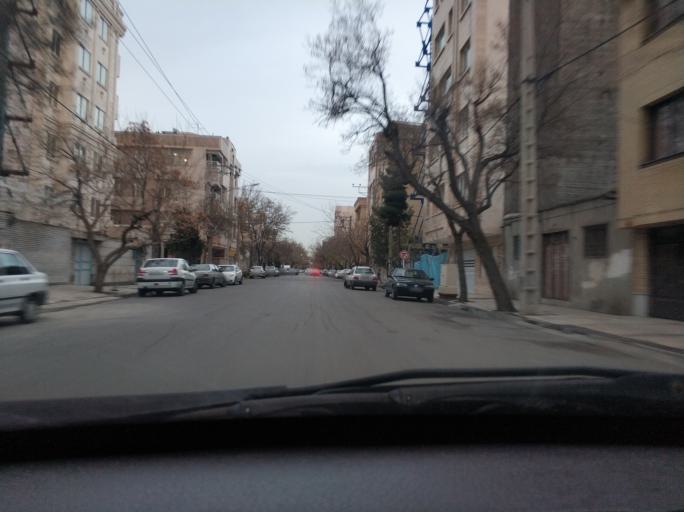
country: IR
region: Razavi Khorasan
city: Mashhad
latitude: 36.2739
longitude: 59.5968
